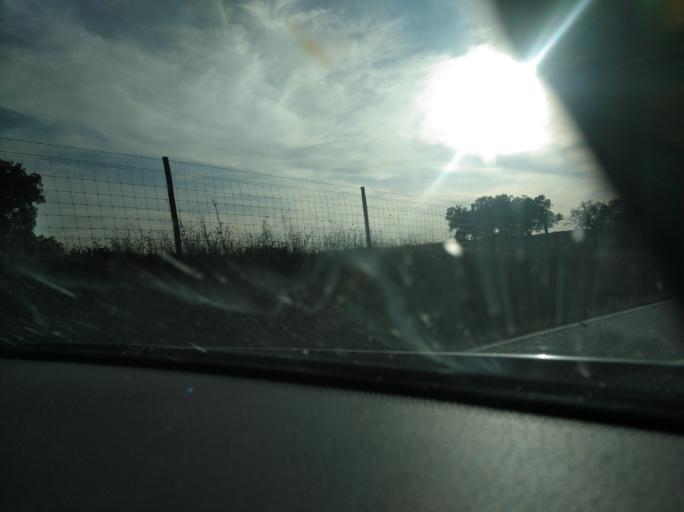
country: PT
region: Evora
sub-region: Estremoz
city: Estremoz
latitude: 38.9600
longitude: -7.5688
